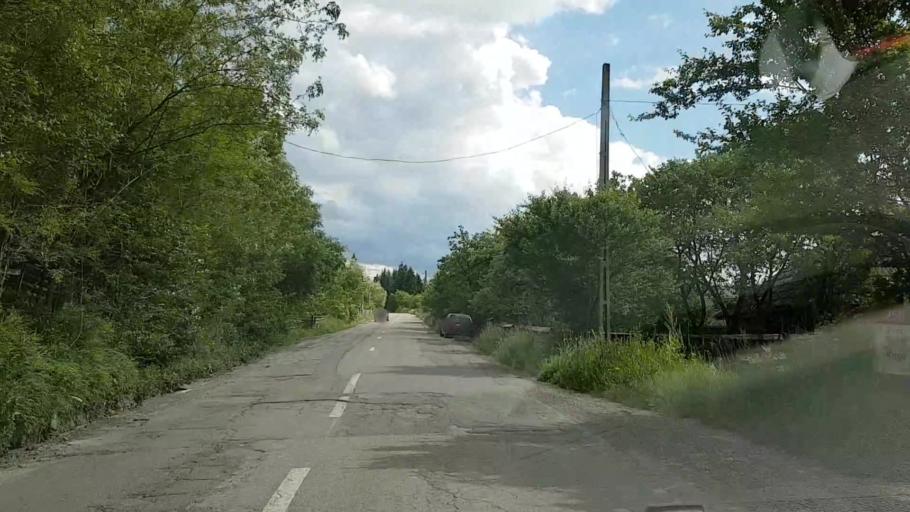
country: RO
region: Neamt
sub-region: Comuna Hangu
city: Hangu
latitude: 47.0576
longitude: 26.0374
